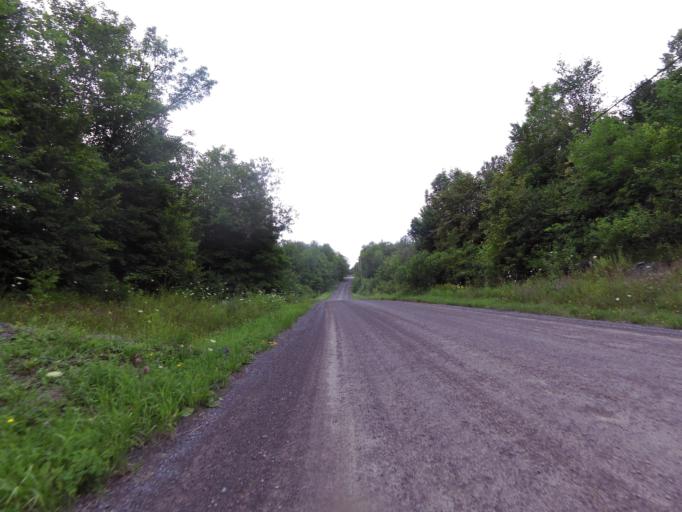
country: CA
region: Ontario
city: Carleton Place
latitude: 45.1675
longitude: -76.2774
